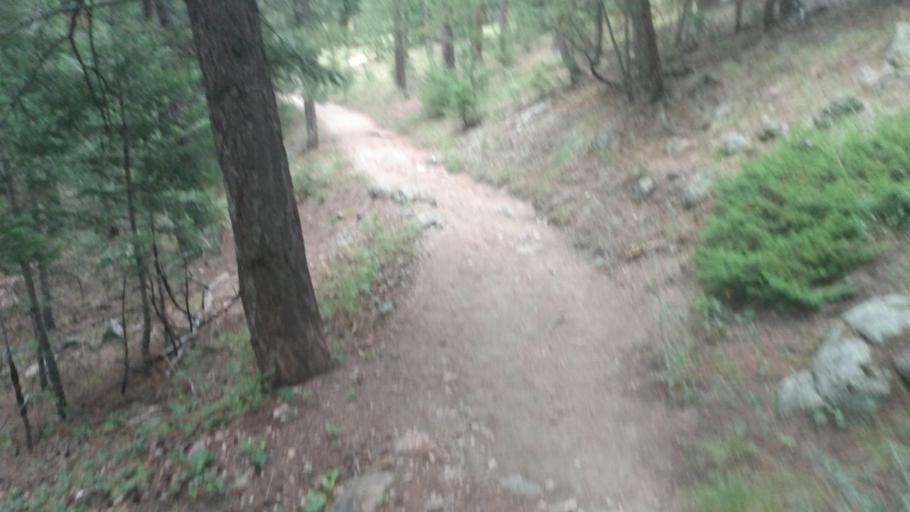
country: US
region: Colorado
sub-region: Boulder County
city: Boulder
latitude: 40.0028
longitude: -105.3073
